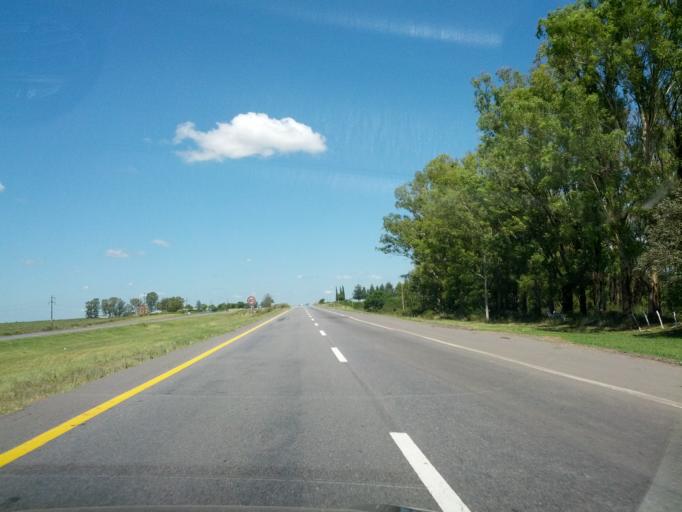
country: AR
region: Entre Rios
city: Gualeguaychu
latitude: -33.1010
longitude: -58.6443
